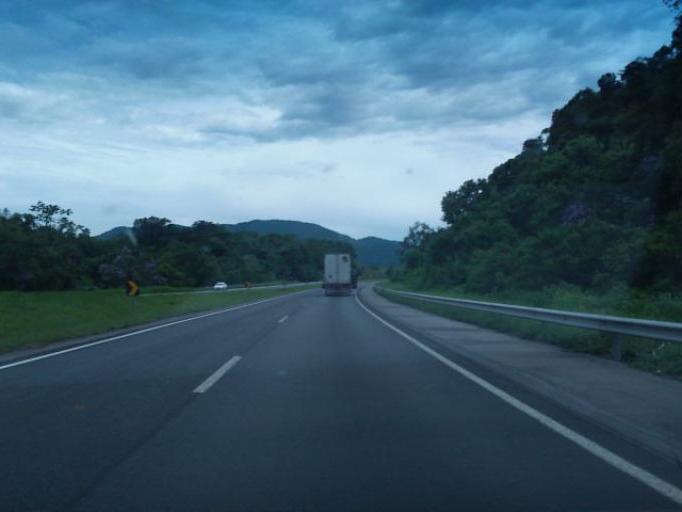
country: BR
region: Sao Paulo
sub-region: Miracatu
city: Miracatu
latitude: -24.2369
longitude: -47.3610
